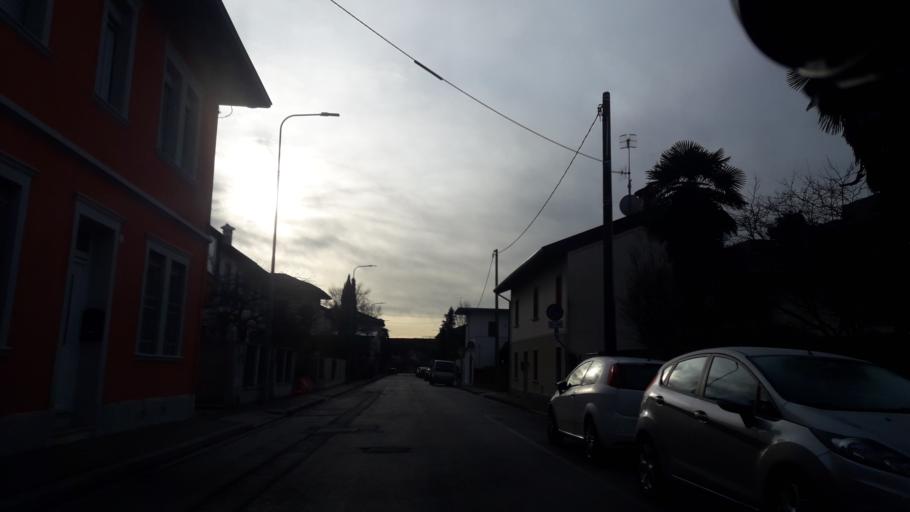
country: IT
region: Friuli Venezia Giulia
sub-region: Provincia di Udine
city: Udine
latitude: 46.0731
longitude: 13.2466
